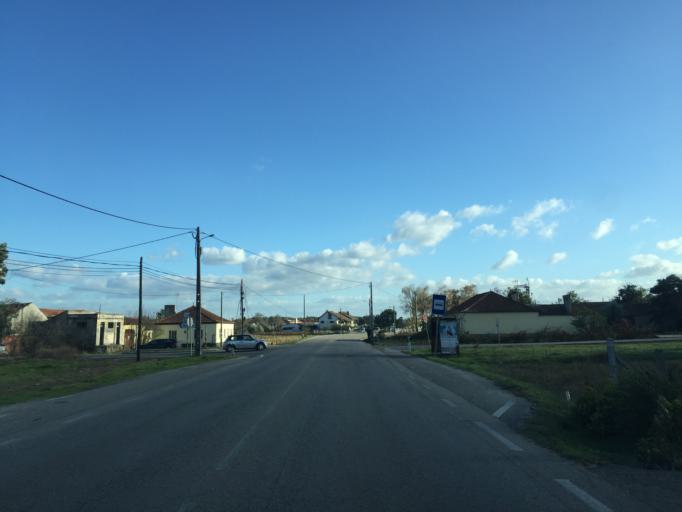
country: PT
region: Leiria
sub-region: Pombal
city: Lourical
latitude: 39.9597
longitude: -8.7875
